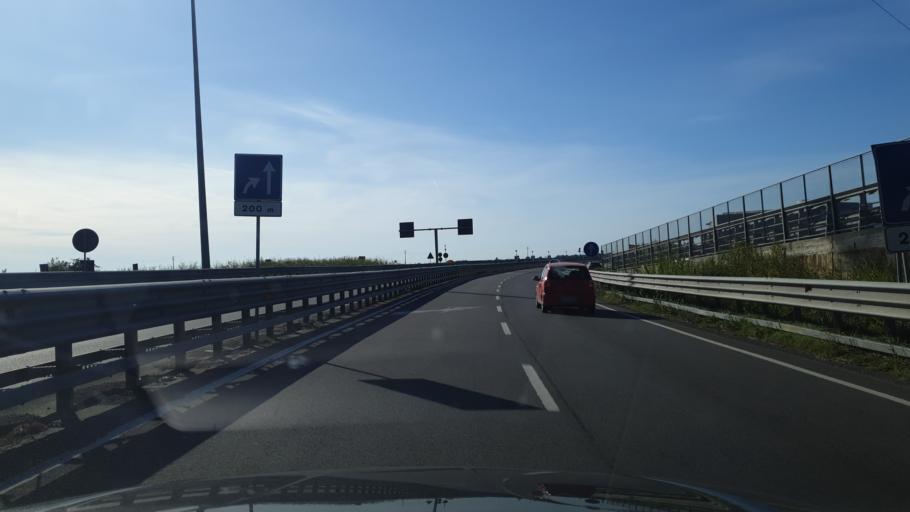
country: IT
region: Emilia-Romagna
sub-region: Provincia di Ravenna
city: Savio
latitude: 44.2899
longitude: 12.3049
